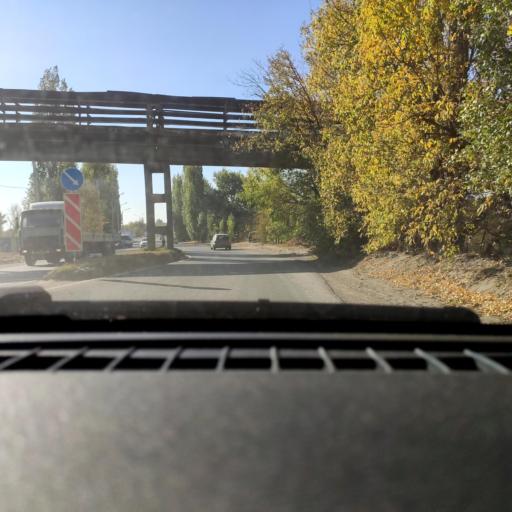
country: RU
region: Voronezj
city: Maslovka
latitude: 51.6249
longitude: 39.2610
